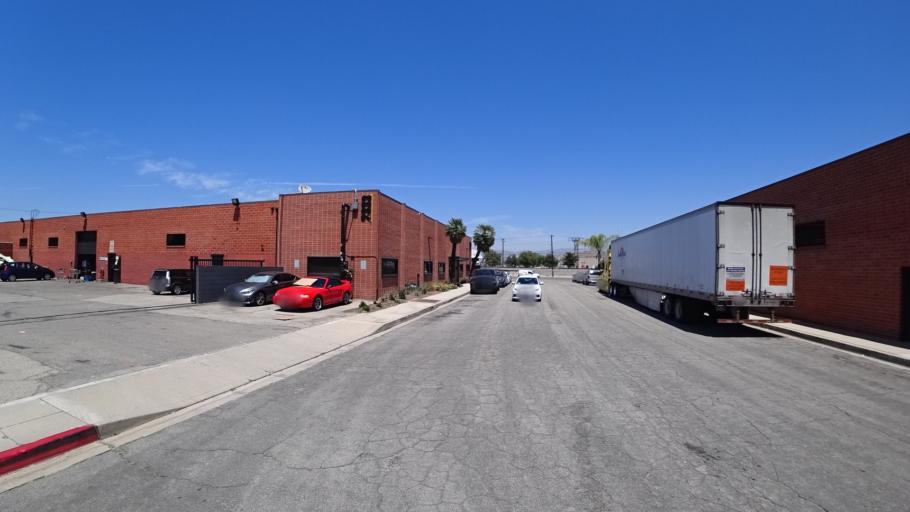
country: US
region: California
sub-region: Los Angeles County
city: North Hollywood
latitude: 34.1928
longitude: -118.3577
